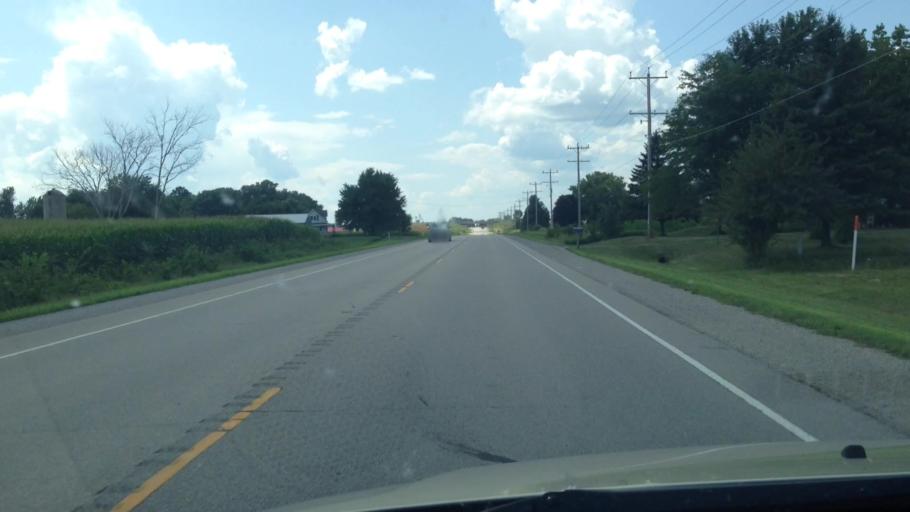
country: US
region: Wisconsin
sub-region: Brown County
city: Pulaski
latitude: 44.6735
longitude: -88.2951
